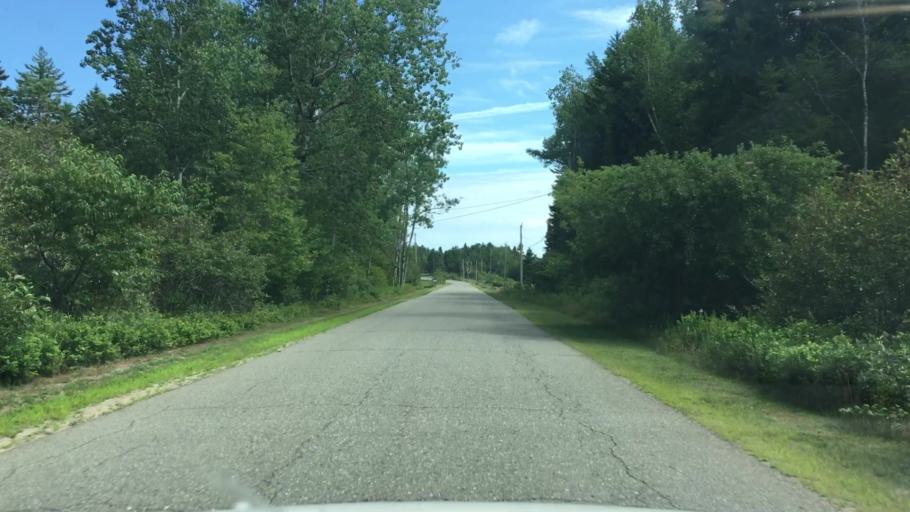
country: US
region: Maine
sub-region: Washington County
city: Eastport
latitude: 44.9307
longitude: -67.0411
